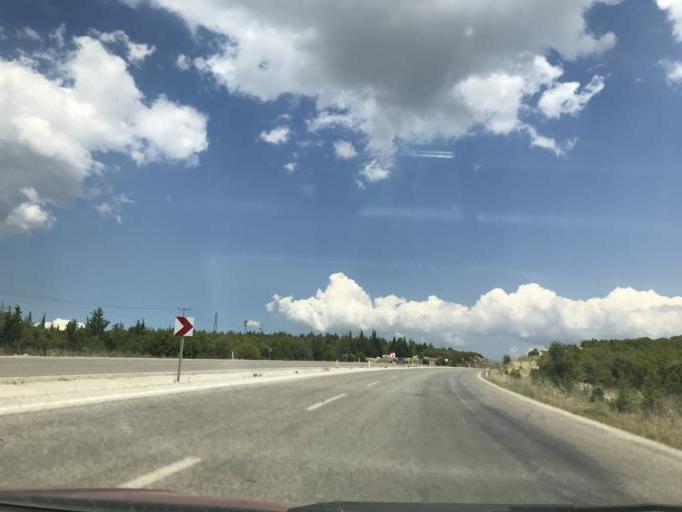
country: TR
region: Denizli
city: Tavas
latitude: 37.5926
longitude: 29.1101
